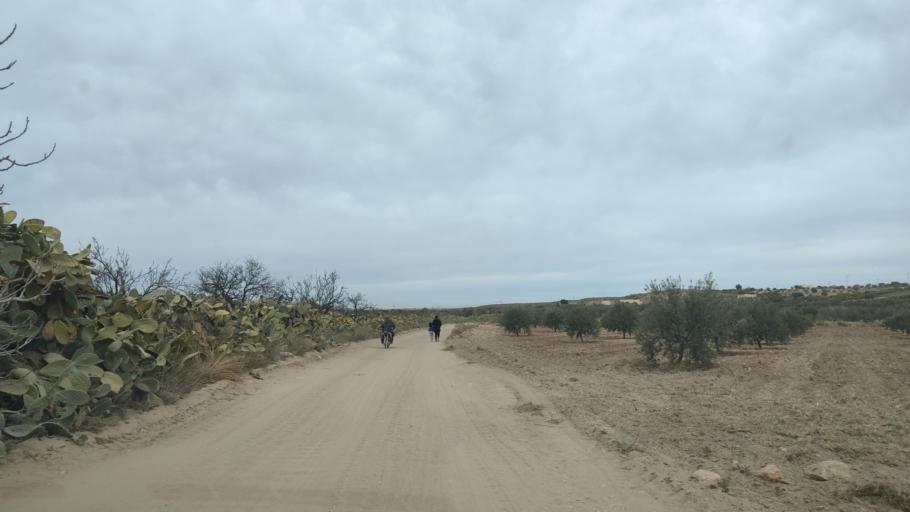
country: TN
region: Al Qasrayn
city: Kasserine
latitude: 35.2433
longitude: 8.9173
